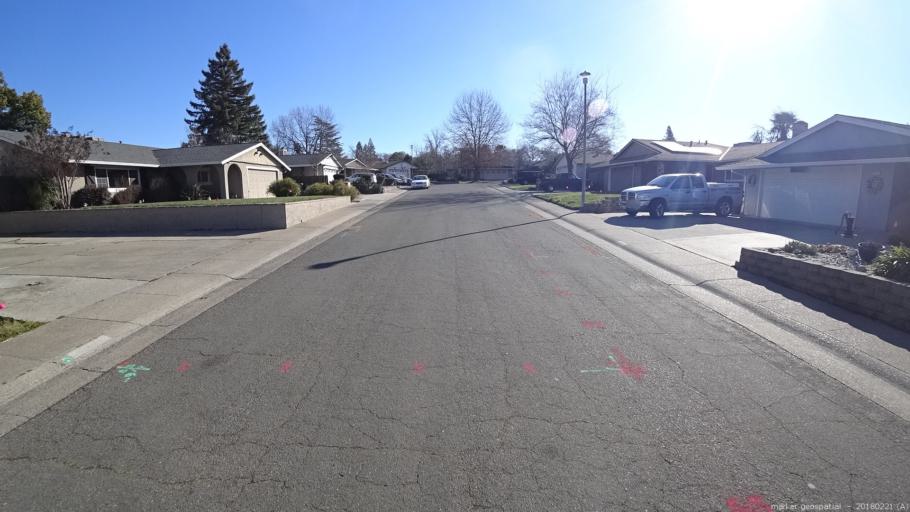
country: US
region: California
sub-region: Sacramento County
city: Orangevale
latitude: 38.6816
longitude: -121.2488
